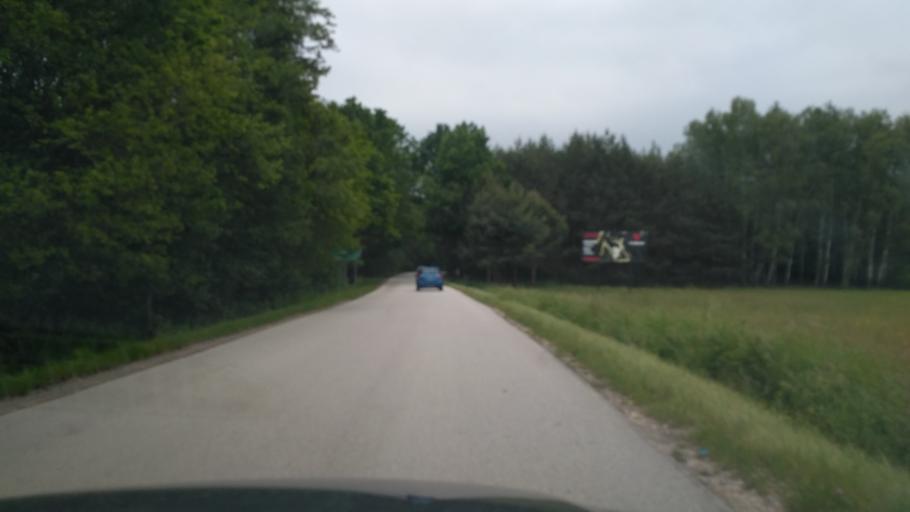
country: PL
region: Subcarpathian Voivodeship
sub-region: Powiat ropczycko-sedziszowski
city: Sedziszow Malopolski
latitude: 50.1243
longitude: 21.6725
